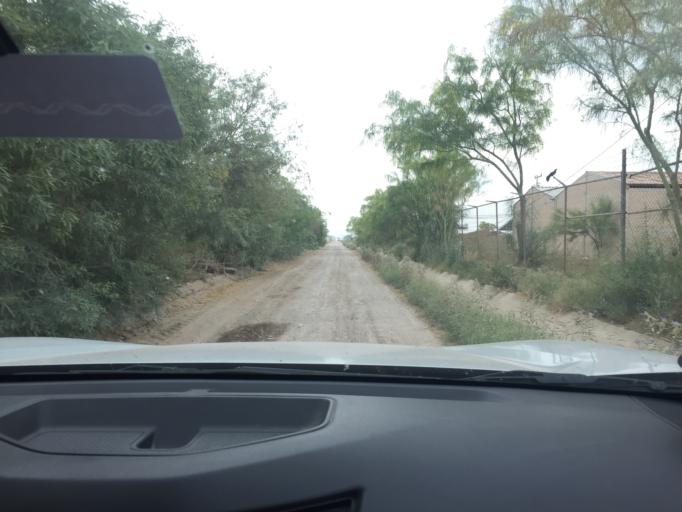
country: MX
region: Durango
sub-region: Gomez Palacio
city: San Jose de Vinedo
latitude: 25.6702
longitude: -103.4400
